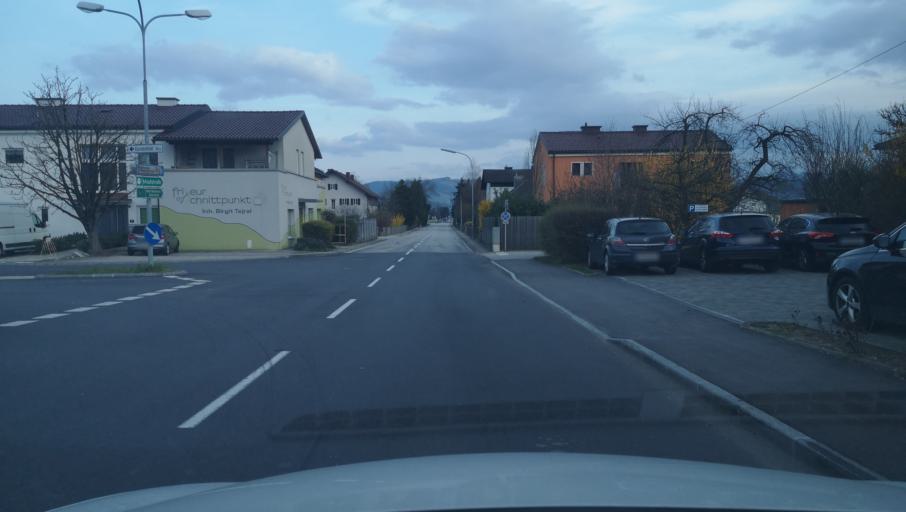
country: AT
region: Lower Austria
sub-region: Politischer Bezirk Amstetten
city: Winklarn
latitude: 48.0764
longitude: 14.8265
